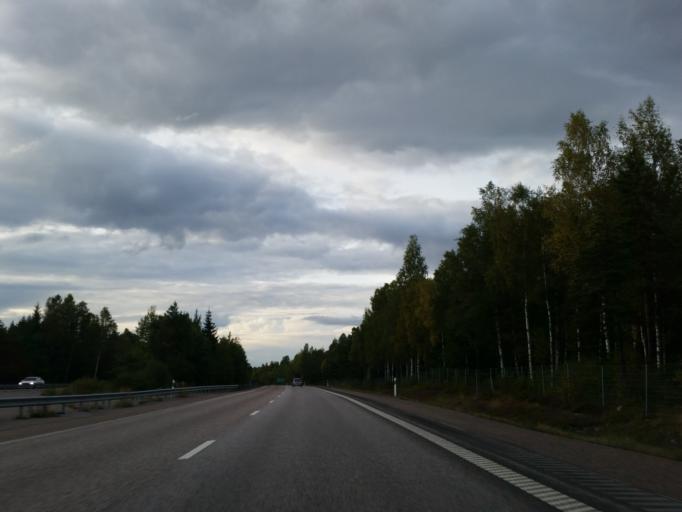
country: SE
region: Stockholm
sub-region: Sigtuna Kommun
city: Marsta
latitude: 59.6955
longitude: 17.8660
